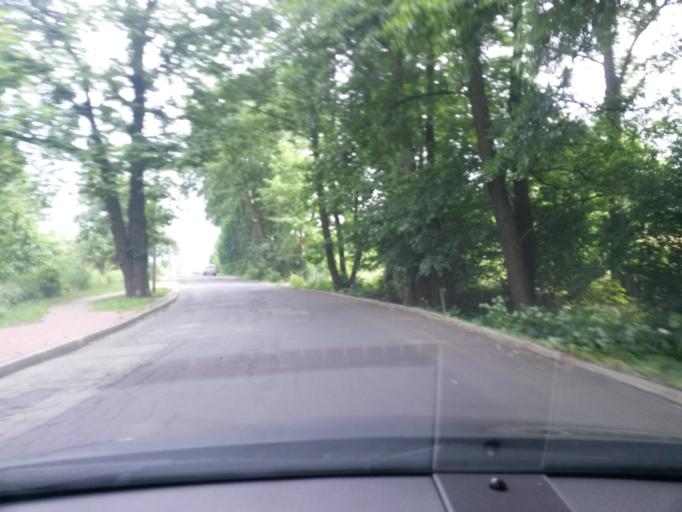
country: PL
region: Silesian Voivodeship
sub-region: Powiat czestochowski
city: Huta Stara B
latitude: 50.7622
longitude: 19.1549
